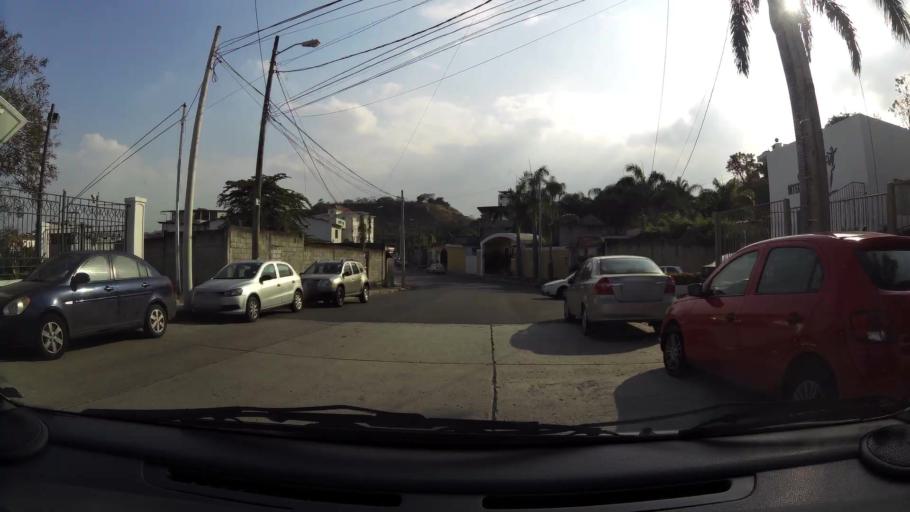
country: EC
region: Guayas
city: Guayaquil
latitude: -2.1564
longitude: -79.9061
